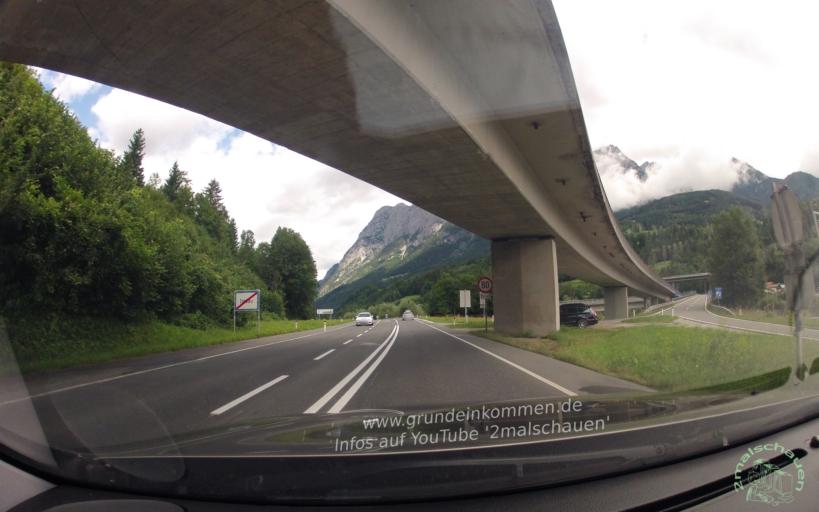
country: AT
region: Salzburg
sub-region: Politischer Bezirk Sankt Johann im Pongau
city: Pfarrwerfen
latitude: 47.4653
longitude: 13.1977
